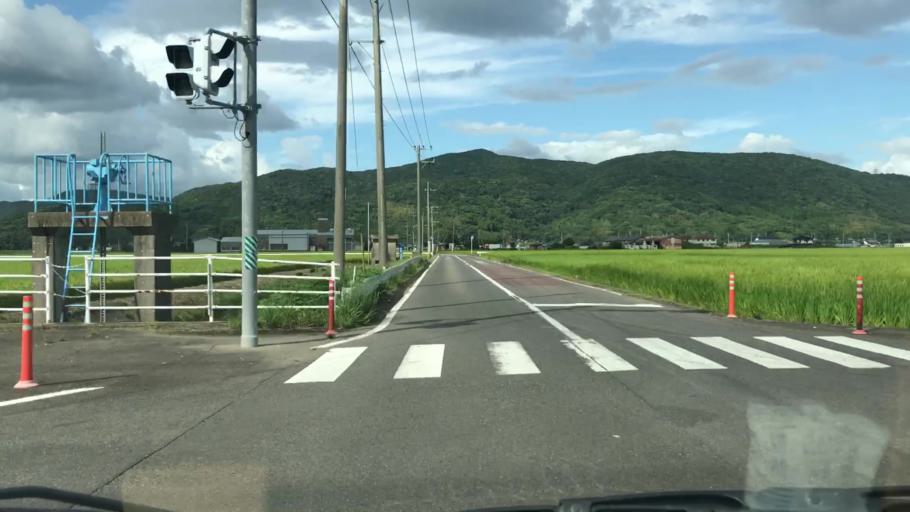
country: JP
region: Saga Prefecture
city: Kashima
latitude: 33.1196
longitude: 130.0707
